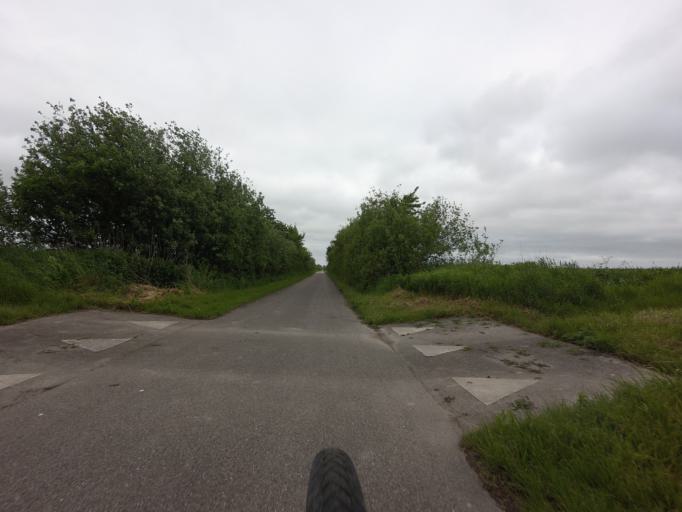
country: DK
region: Zealand
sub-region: Slagelse Kommune
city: Skaelskor
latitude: 55.2641
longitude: 11.3996
